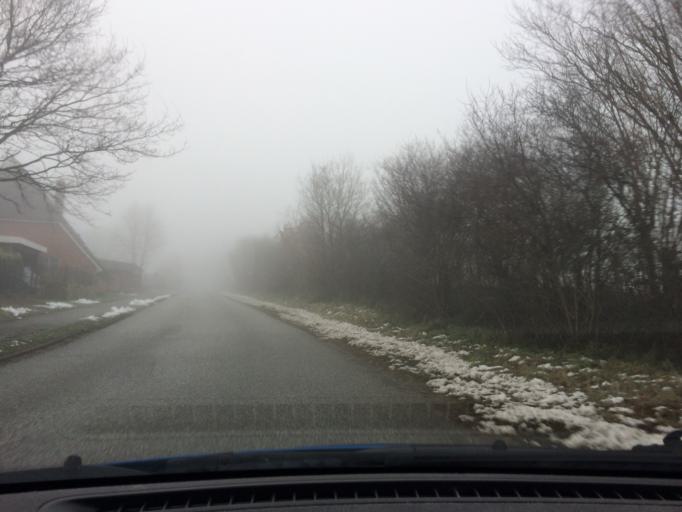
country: DE
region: Schleswig-Holstein
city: Juliusburg
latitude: 53.4193
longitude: 10.5063
